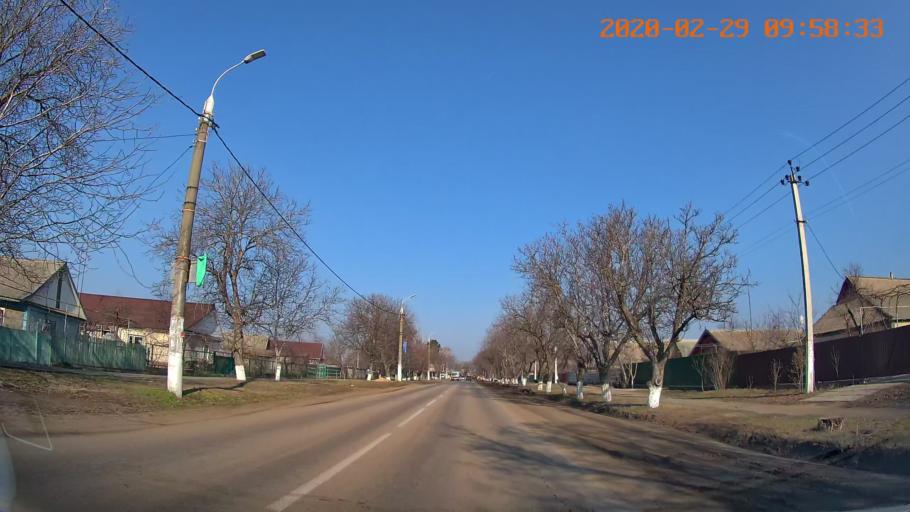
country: MD
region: Telenesti
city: Slobozia
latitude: 46.7497
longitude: 29.6910
